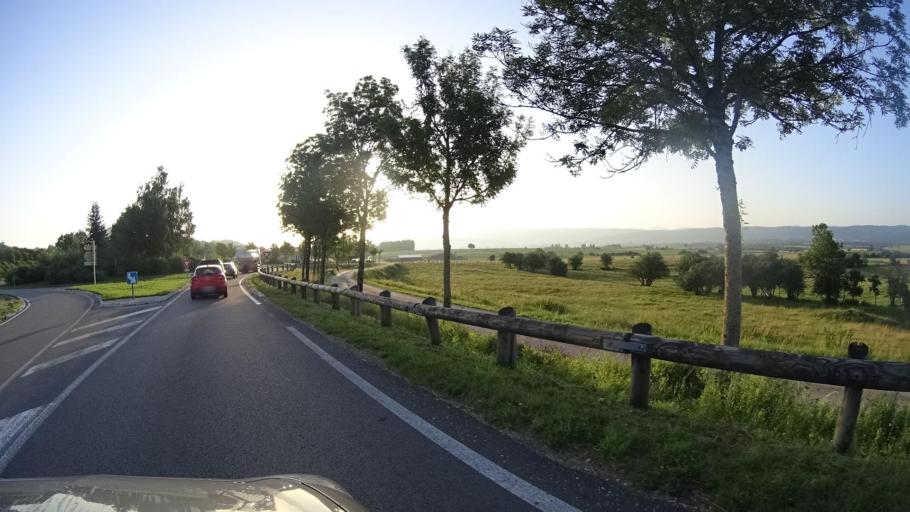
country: FR
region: Franche-Comte
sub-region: Departement du Doubs
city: Doubs
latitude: 46.9090
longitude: 6.2670
